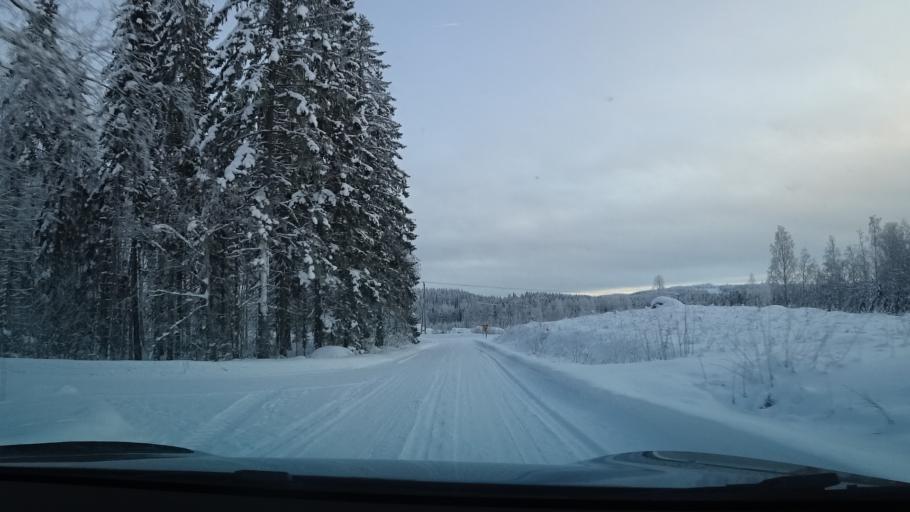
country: FI
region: North Karelia
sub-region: Pielisen Karjala
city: Lieksa
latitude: 63.1034
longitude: 29.7567
